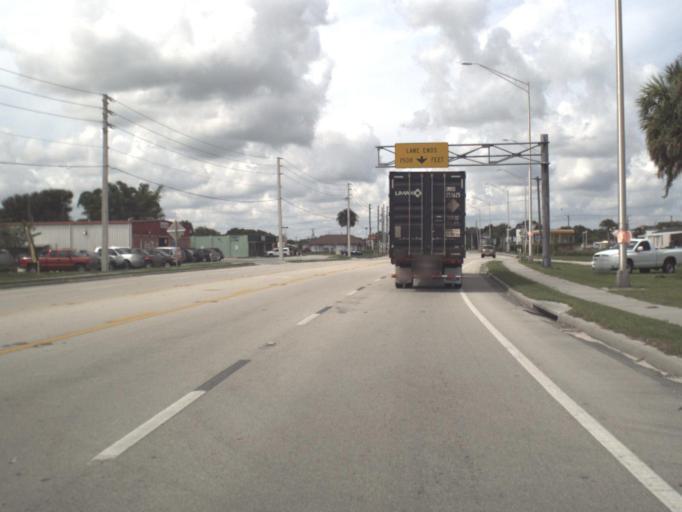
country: US
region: Florida
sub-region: Okeechobee County
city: Okeechobee
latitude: 27.2435
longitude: -80.8454
